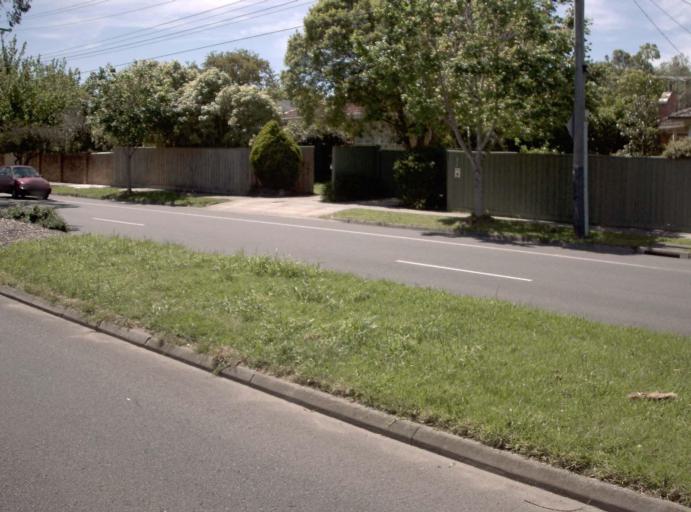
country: AU
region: Victoria
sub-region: Whitehorse
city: Blackburn South
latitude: -37.8447
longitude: 145.1546
